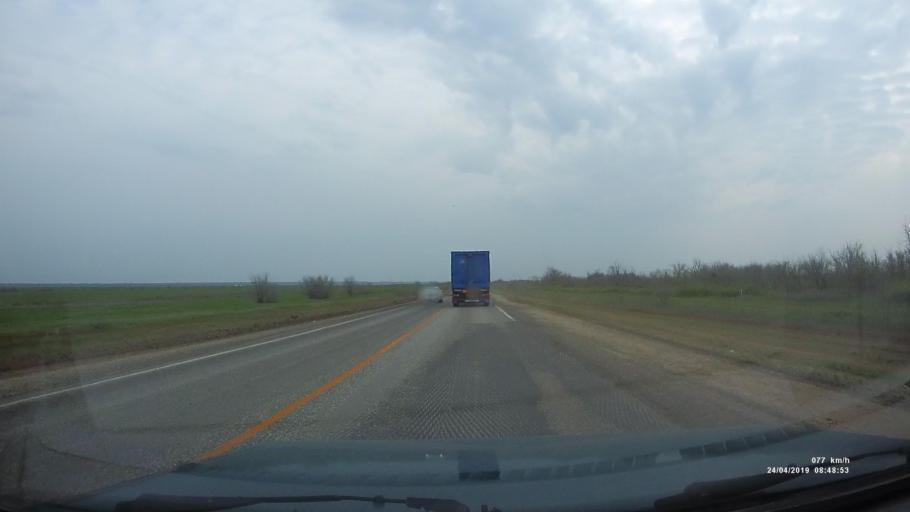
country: RU
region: Kalmykiya
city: Arshan'
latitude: 46.2537
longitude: 44.1160
